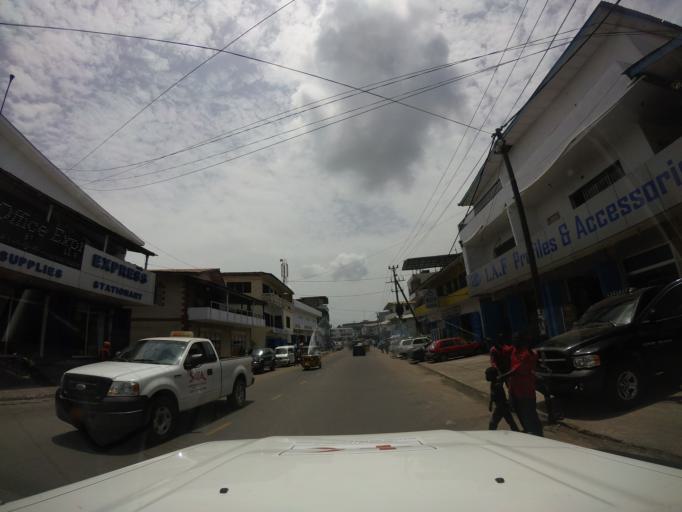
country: LR
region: Montserrado
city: Monrovia
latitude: 6.3067
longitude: -10.8003
